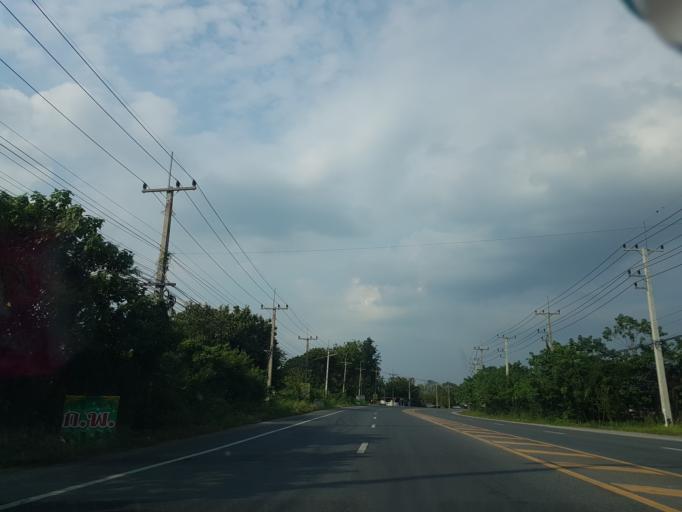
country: TH
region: Sara Buri
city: Phra Phutthabat
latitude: 14.6715
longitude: 100.7733
